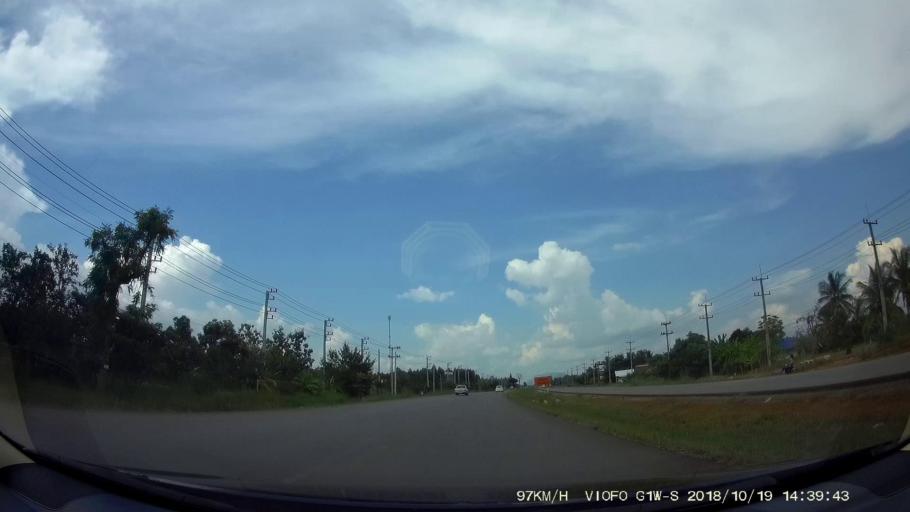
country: TH
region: Chaiyaphum
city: Kaeng Khro
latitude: 16.2299
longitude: 102.1946
